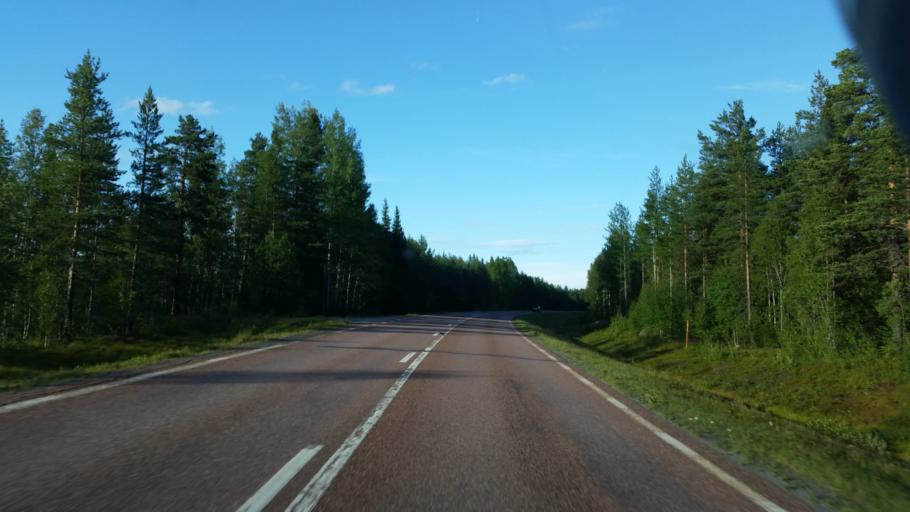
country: SE
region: Jaemtland
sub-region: Stroemsunds Kommun
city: Stroemsund
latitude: 63.9307
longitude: 15.7622
